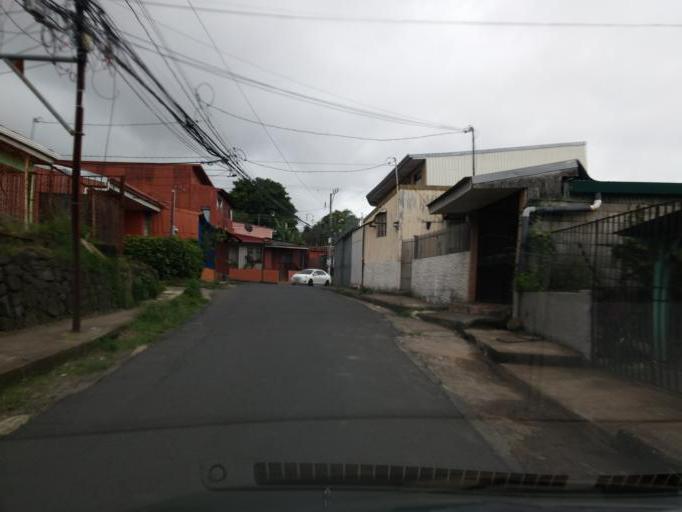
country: CR
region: Heredia
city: Mercedes
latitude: 10.0239
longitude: -84.1276
